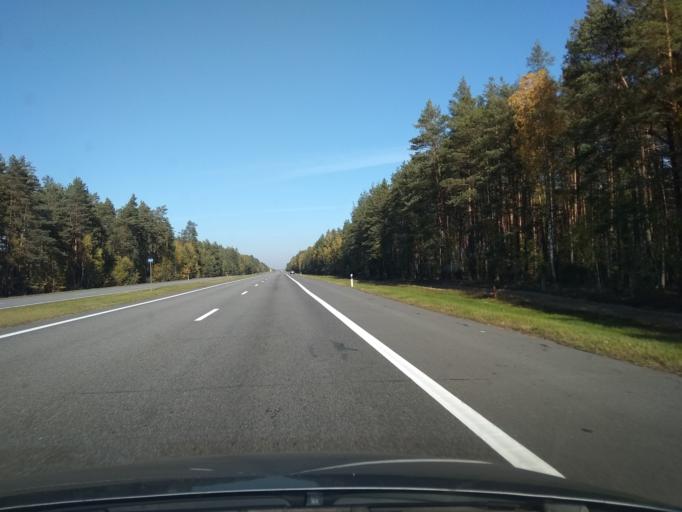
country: BY
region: Grodnenskaya
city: Zhyrovichy
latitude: 52.8828
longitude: 25.6648
